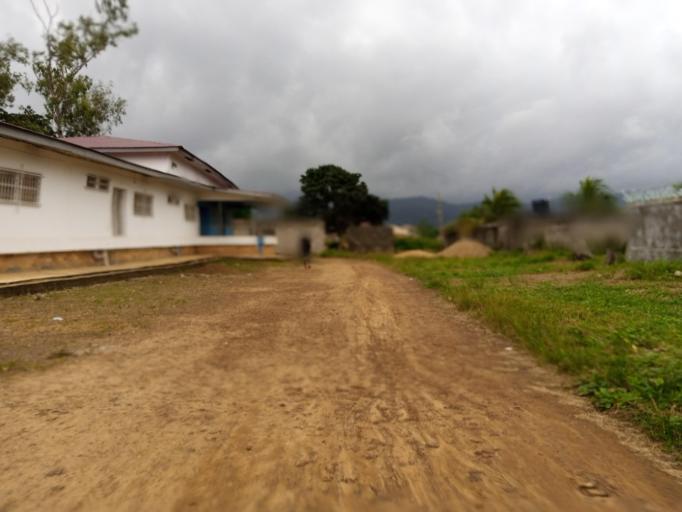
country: SL
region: Eastern Province
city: Kenema
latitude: 7.8748
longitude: -11.1780
